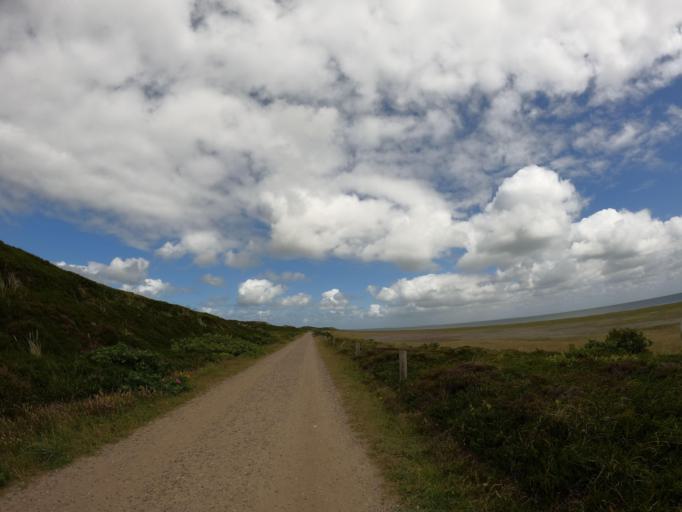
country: DE
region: Schleswig-Holstein
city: Norddorf
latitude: 54.7858
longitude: 8.2895
